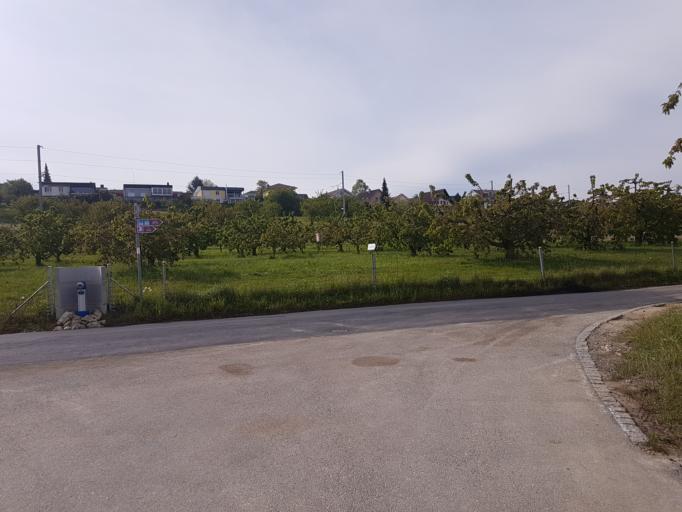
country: CH
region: Bern
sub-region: Seeland District
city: Tauffelen
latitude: 47.0887
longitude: 7.2139
